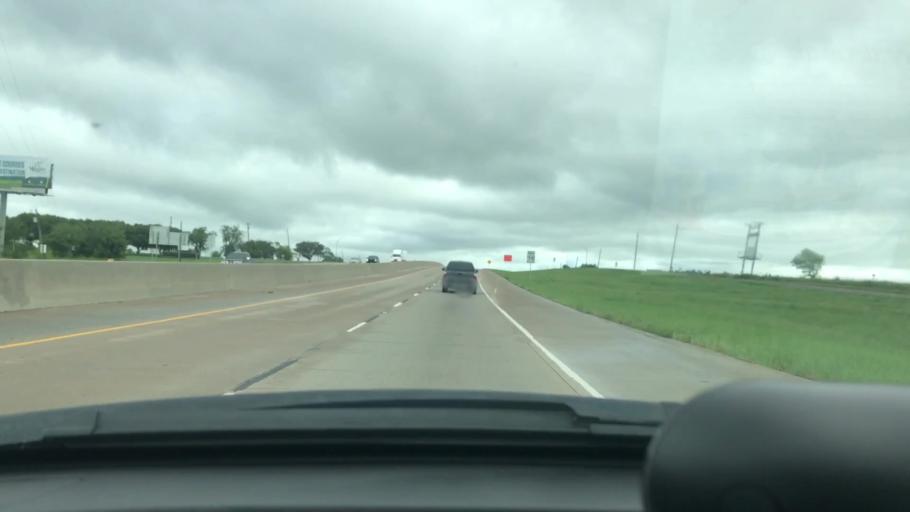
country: US
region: Texas
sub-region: Grayson County
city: Howe
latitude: 33.5303
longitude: -96.6117
